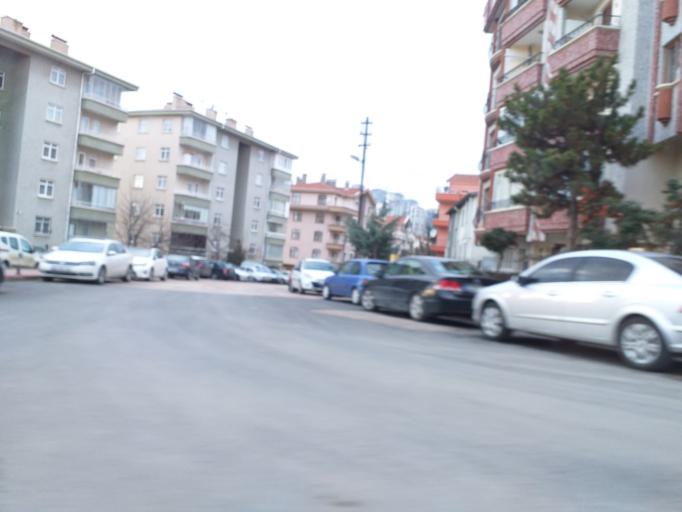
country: TR
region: Ankara
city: Ankara
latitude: 39.9768
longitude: 32.8189
